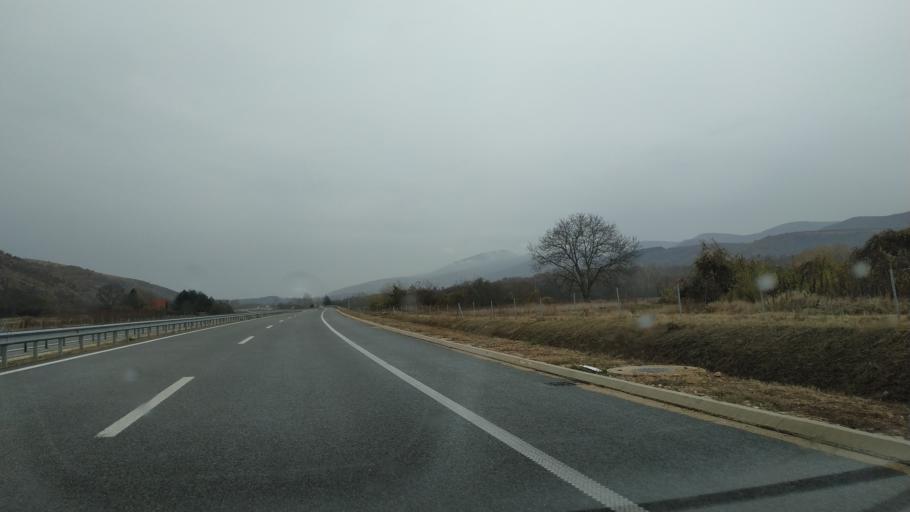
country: RS
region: Central Serbia
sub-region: Pirotski Okrug
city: Bela Palanka
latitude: 43.2349
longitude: 22.3644
